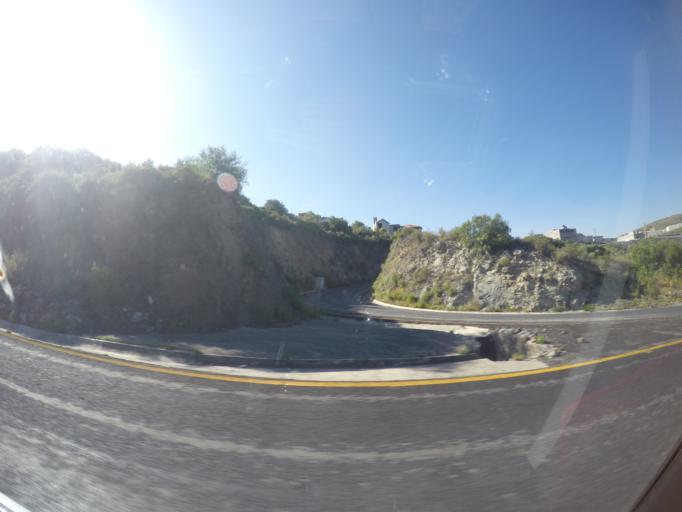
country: MX
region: Hidalgo
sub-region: Mineral de la Reforma
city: Colonia Militar
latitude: 20.1204
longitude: -98.7033
